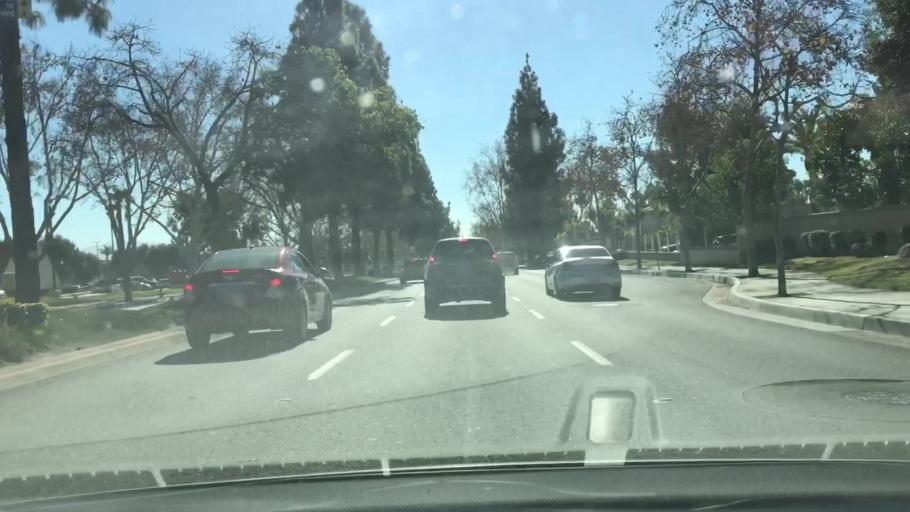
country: US
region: California
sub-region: San Bernardino County
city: Chino
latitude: 34.0377
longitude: -117.6896
